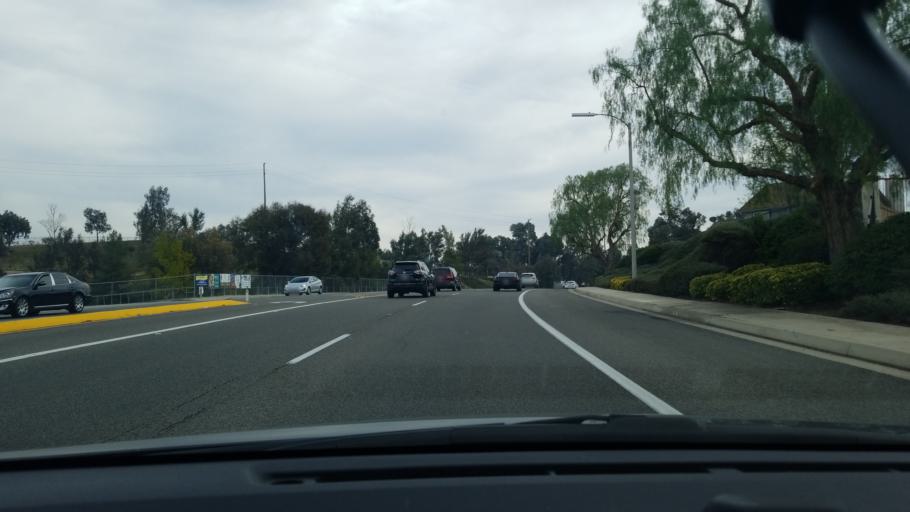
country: US
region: California
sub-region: Riverside County
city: Temecula
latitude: 33.5159
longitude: -117.1267
